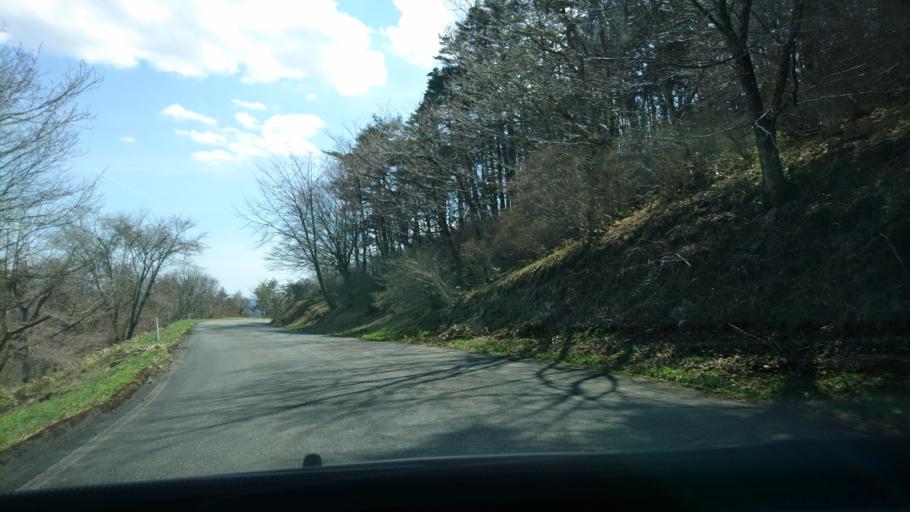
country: JP
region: Iwate
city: Ofunato
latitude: 38.9727
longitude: 141.4562
